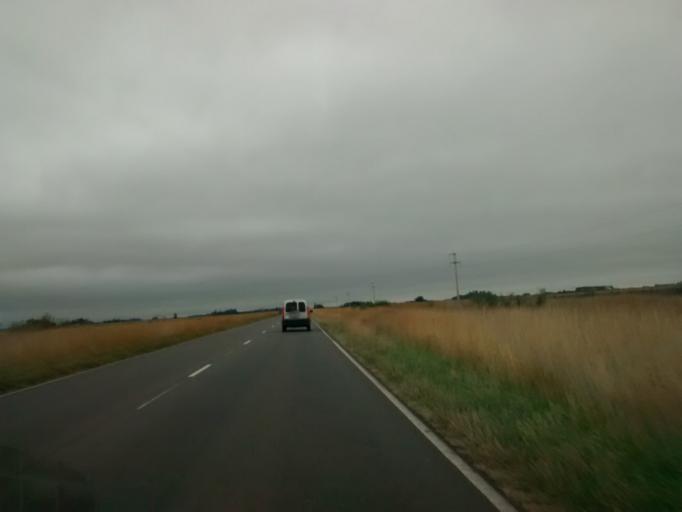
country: AR
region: Buenos Aires
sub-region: Partido de Ayacucho
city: Ayacucho
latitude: -37.0148
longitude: -58.5379
